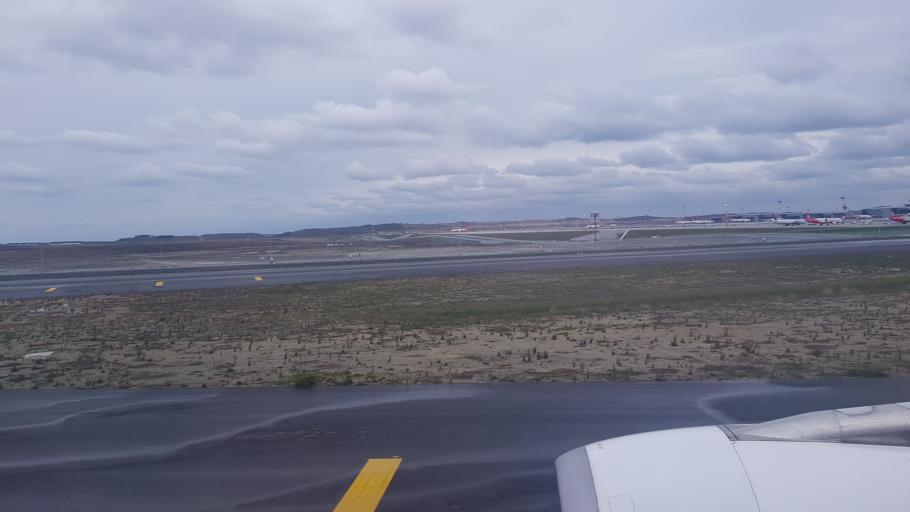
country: TR
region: Istanbul
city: Durusu
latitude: 41.2801
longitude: 28.7278
